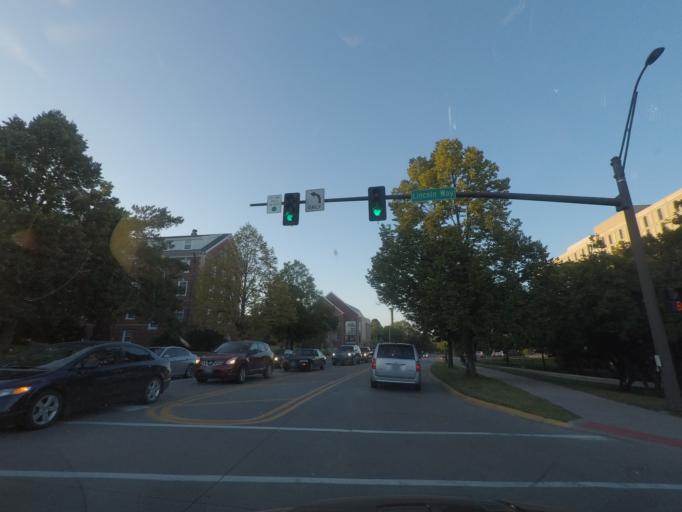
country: US
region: Iowa
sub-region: Story County
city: Ames
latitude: 42.0228
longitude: -93.6394
